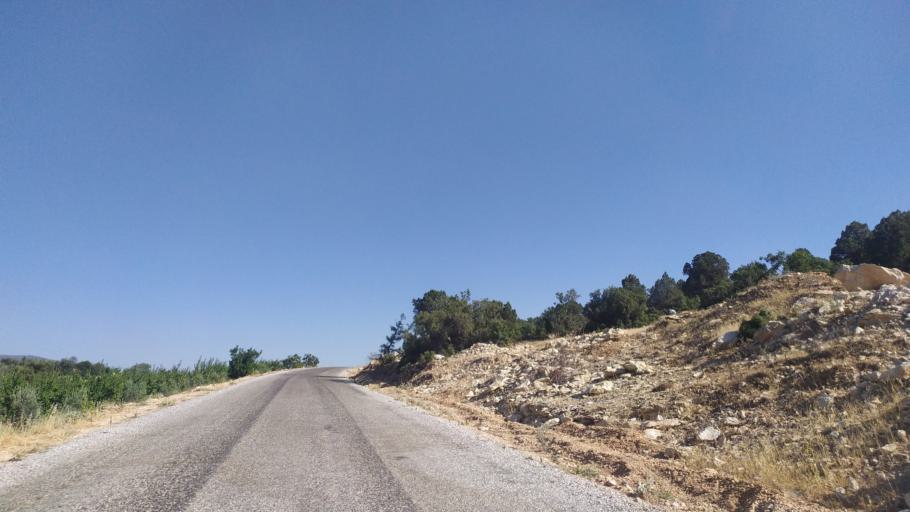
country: TR
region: Mersin
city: Mut
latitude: 36.6998
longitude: 33.4798
